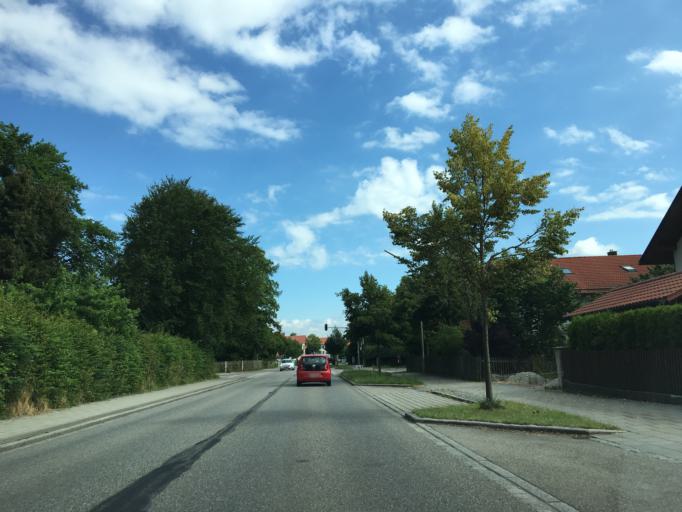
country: DE
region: Bavaria
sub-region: Upper Bavaria
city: Sauerlach
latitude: 47.9689
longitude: 11.6536
